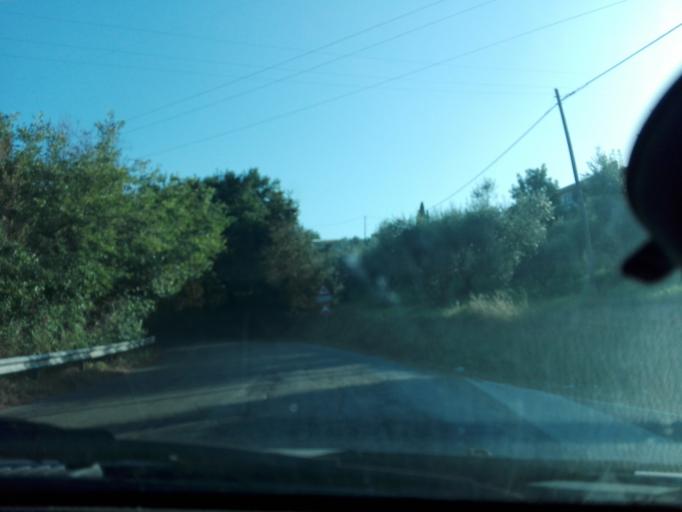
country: IT
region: Abruzzo
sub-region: Provincia di Pescara
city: Cappelle sul Tavo
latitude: 42.4512
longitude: 14.0888
